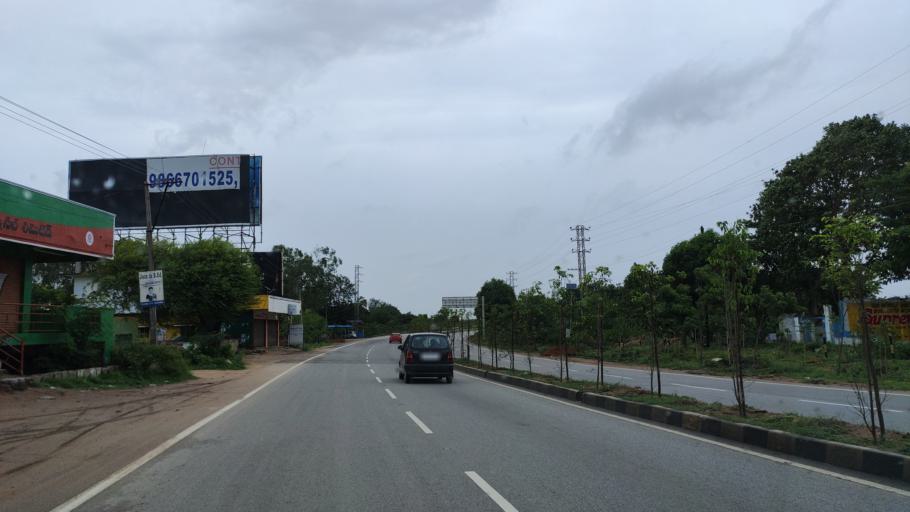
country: IN
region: Telangana
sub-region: Rangareddi
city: Secunderabad
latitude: 17.5998
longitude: 78.5679
